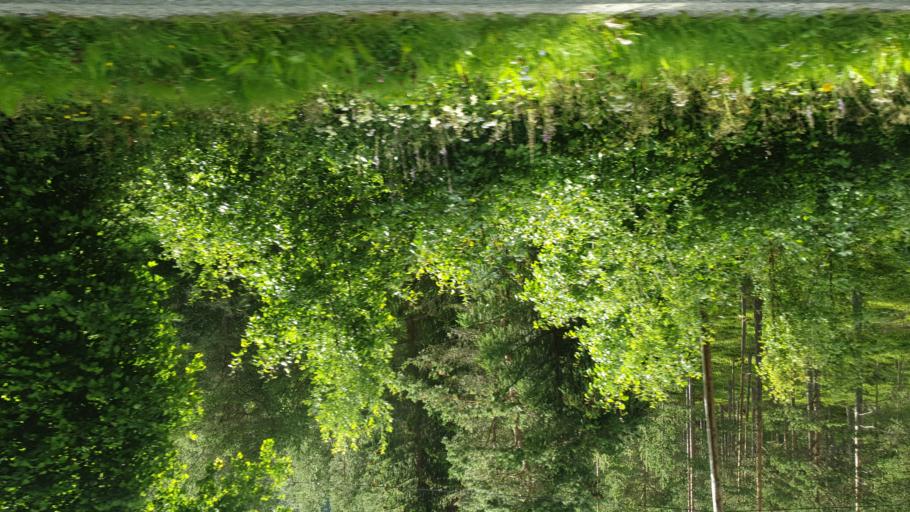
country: NO
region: Oppland
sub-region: Dovre
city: Dovre
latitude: 61.8457
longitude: 9.3338
